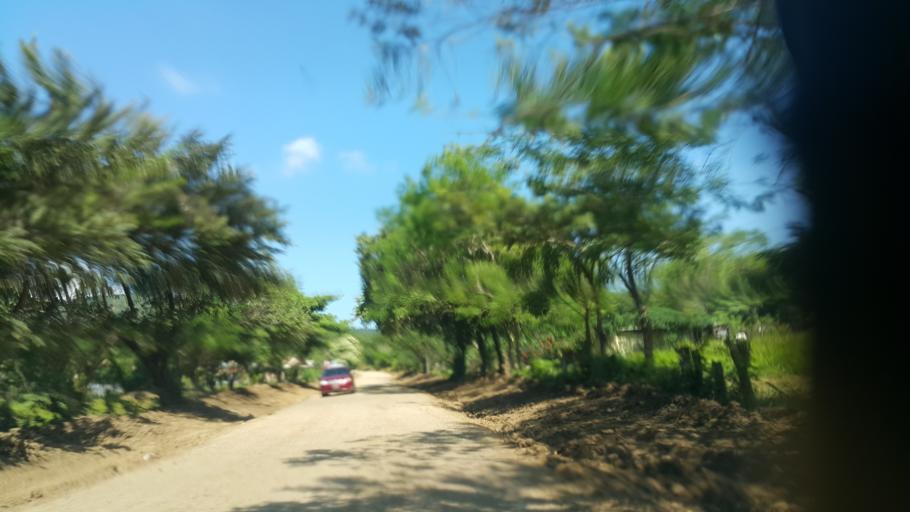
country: NI
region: Rivas
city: San Juan del Sur
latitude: 11.2936
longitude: -85.8891
